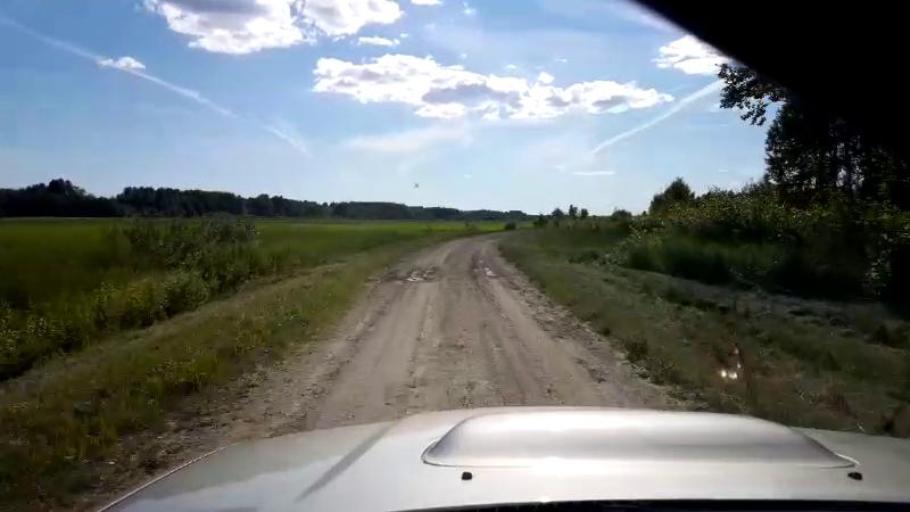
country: EE
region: Paernumaa
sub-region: Sindi linn
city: Sindi
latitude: 58.4929
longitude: 24.6048
